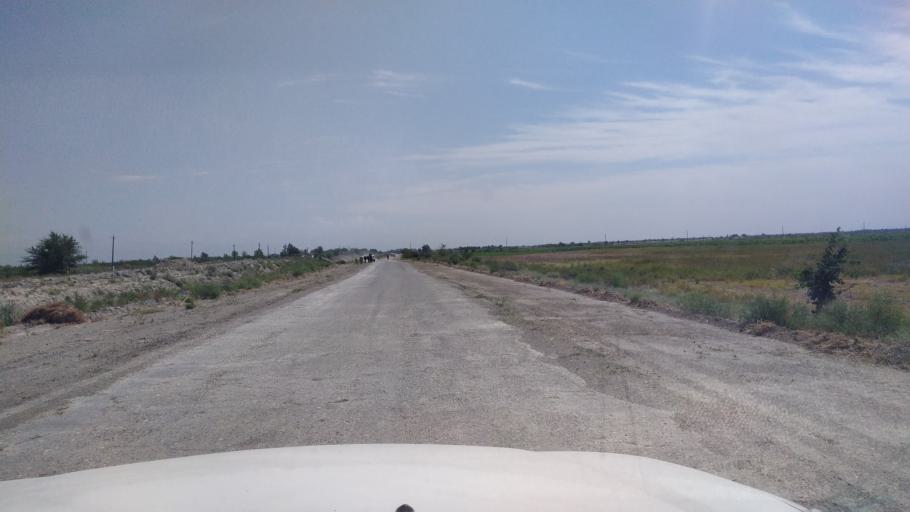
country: UZ
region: Namangan
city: Toshbuloq
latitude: 40.7912
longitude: 71.5699
